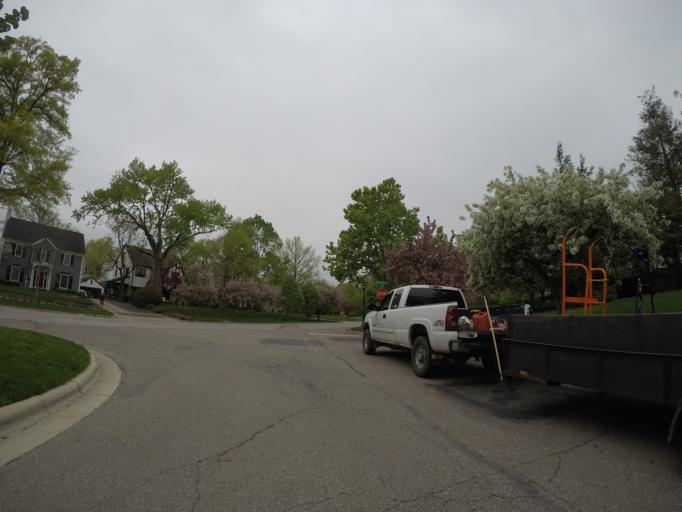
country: US
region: Ohio
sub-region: Franklin County
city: Upper Arlington
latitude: 40.0067
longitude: -83.0656
